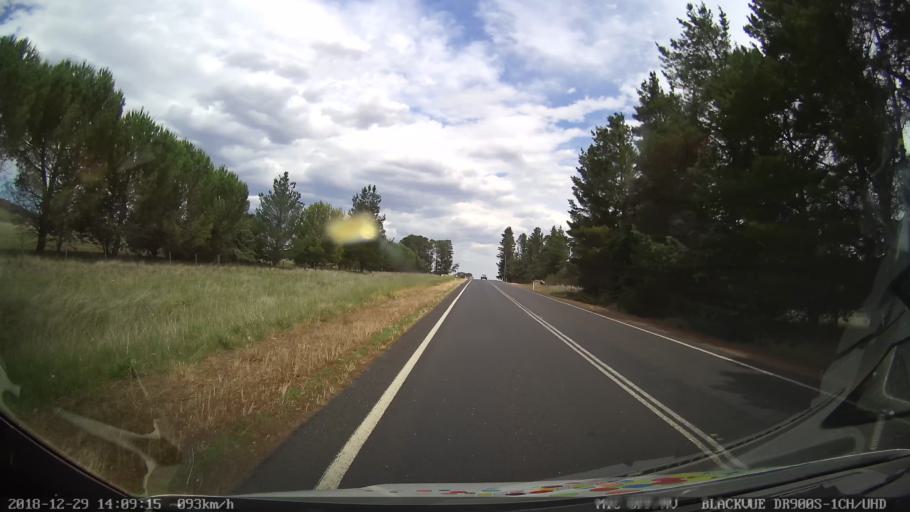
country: AU
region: New South Wales
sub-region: Cooma-Monaro
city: Cooma
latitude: -36.3763
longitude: 149.2128
